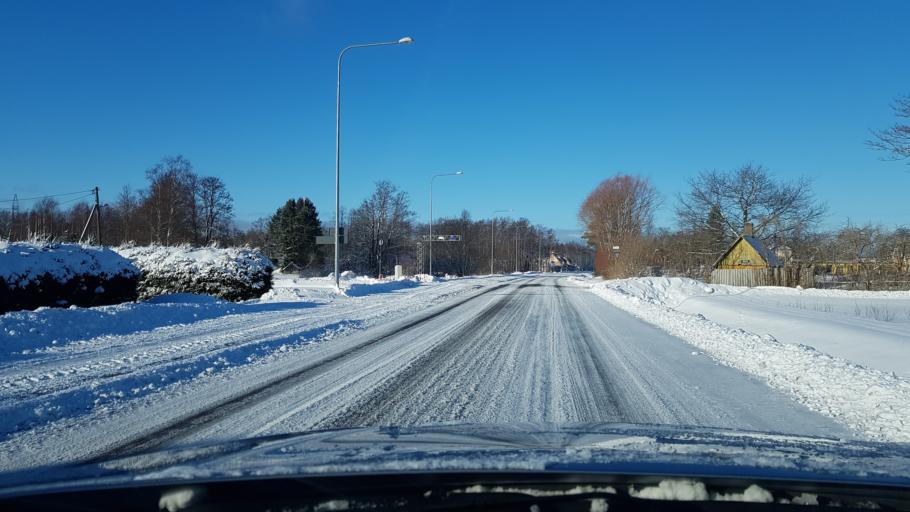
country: EE
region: Hiiumaa
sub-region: Kaerdla linn
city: Kardla
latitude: 58.9854
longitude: 22.7559
